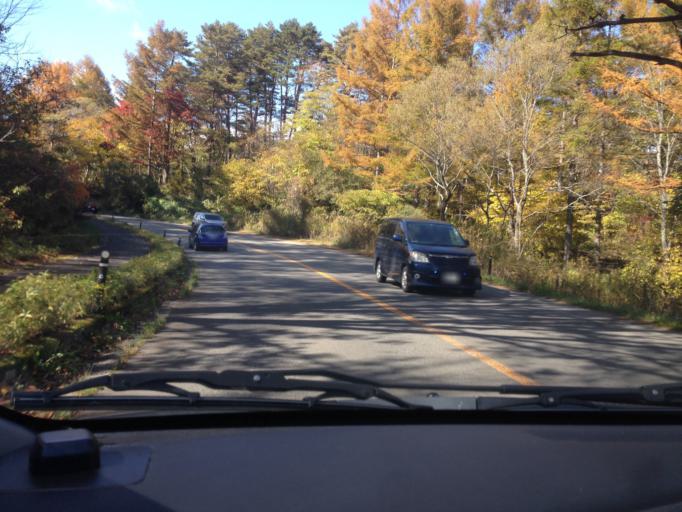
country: JP
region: Fukushima
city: Inawashiro
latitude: 37.6587
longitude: 140.0735
